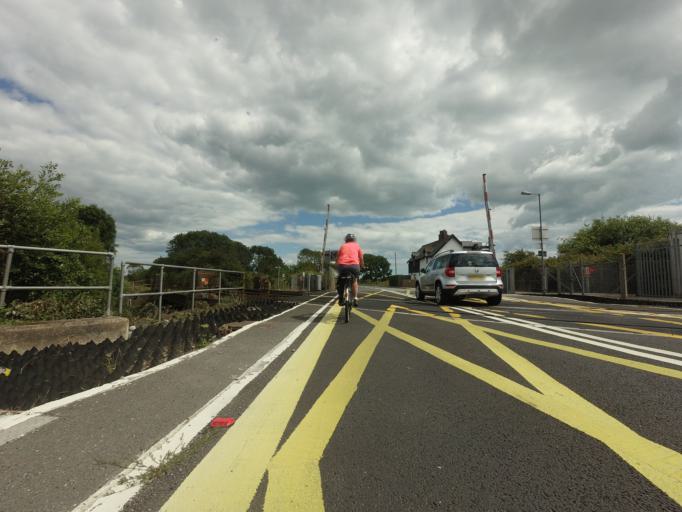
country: GB
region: England
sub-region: East Sussex
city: Pevensey
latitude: 50.8178
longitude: 0.3436
